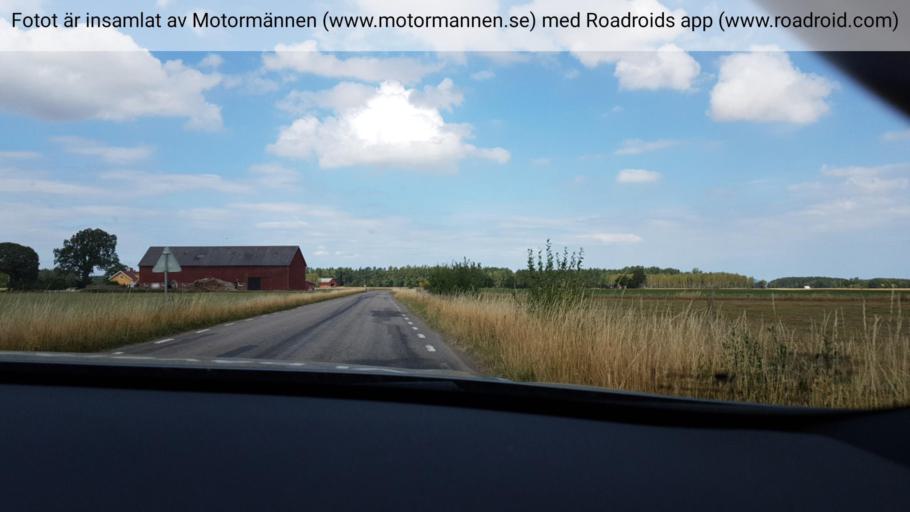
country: SE
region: Vaestra Goetaland
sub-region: Lidkopings Kommun
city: Vinninga
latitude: 58.4455
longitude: 13.3386
